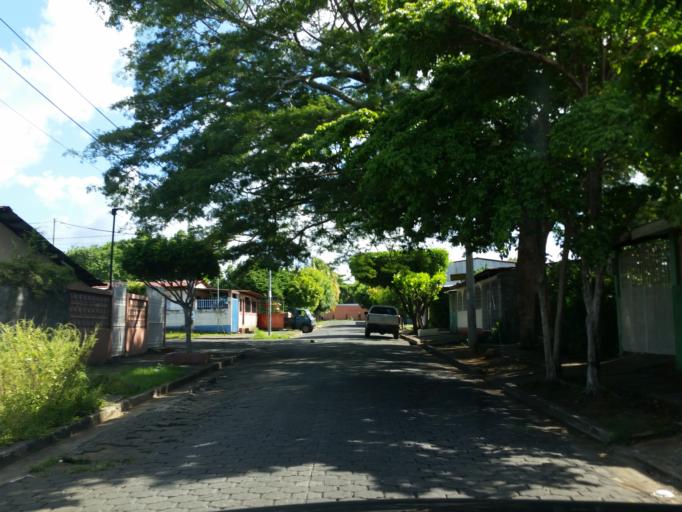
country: NI
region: Managua
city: Managua
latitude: 12.1429
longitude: -86.2412
